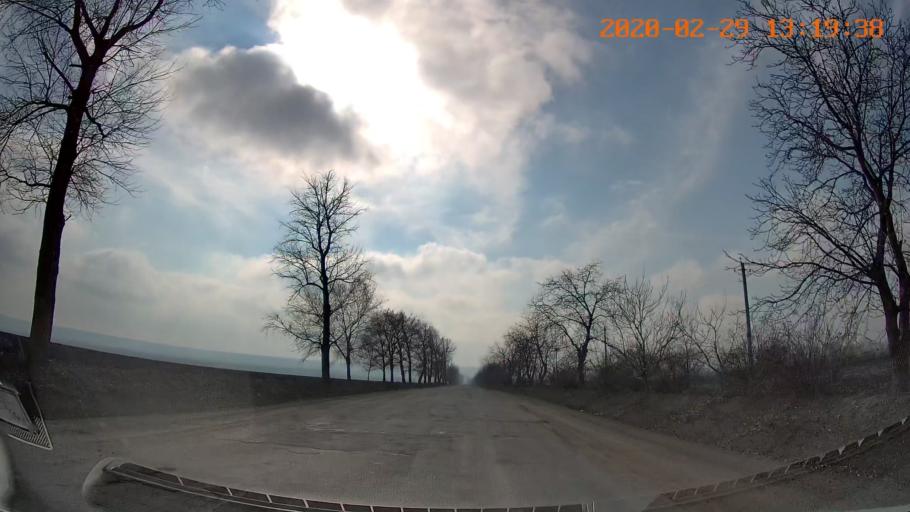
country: MD
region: Telenesti
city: Camenca
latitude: 47.9869
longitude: 28.6494
